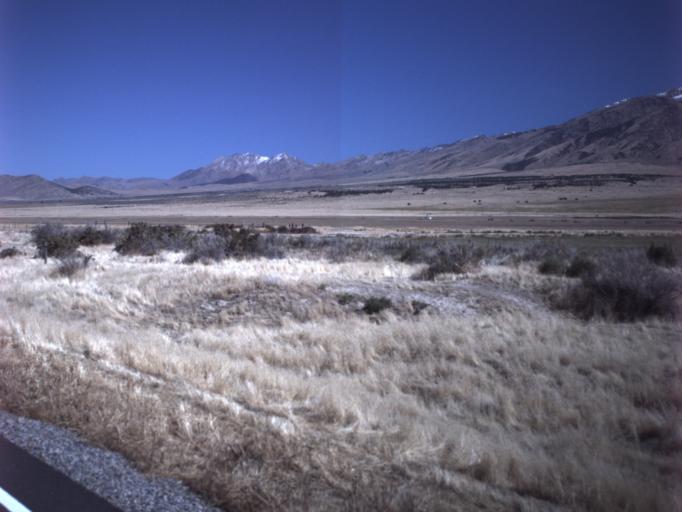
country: US
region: Utah
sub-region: Tooele County
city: Grantsville
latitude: 40.4587
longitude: -112.7475
